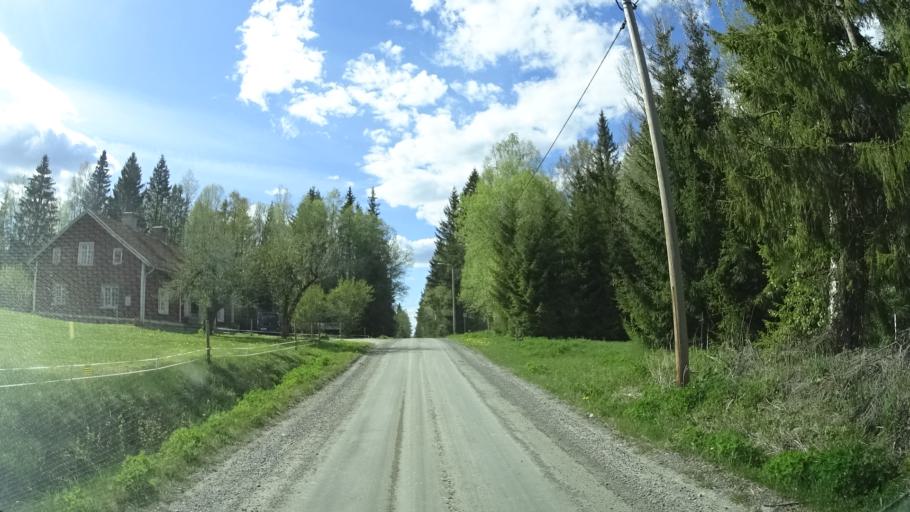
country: SE
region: OErebro
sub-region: Nora Kommun
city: As
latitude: 59.4380
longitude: 14.8547
